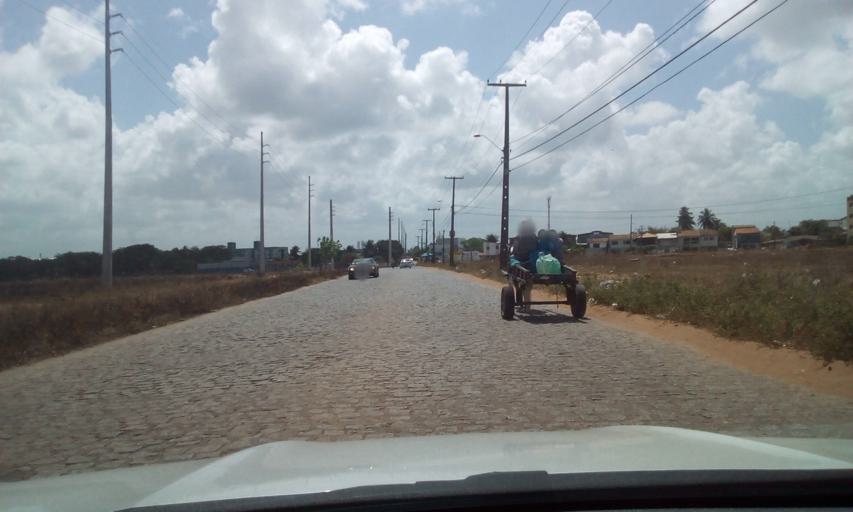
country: BR
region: Paraiba
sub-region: Joao Pessoa
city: Joao Pessoa
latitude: -7.0775
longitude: -34.8443
